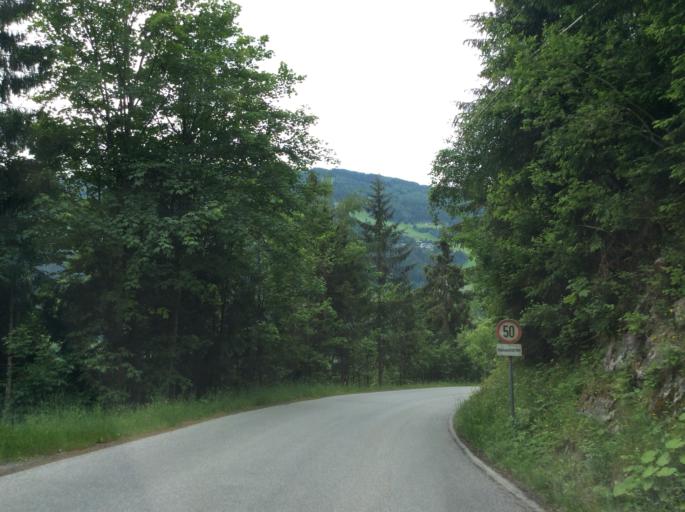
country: AT
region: Styria
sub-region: Politischer Bezirk Liezen
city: Schladming
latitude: 47.4065
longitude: 13.6942
